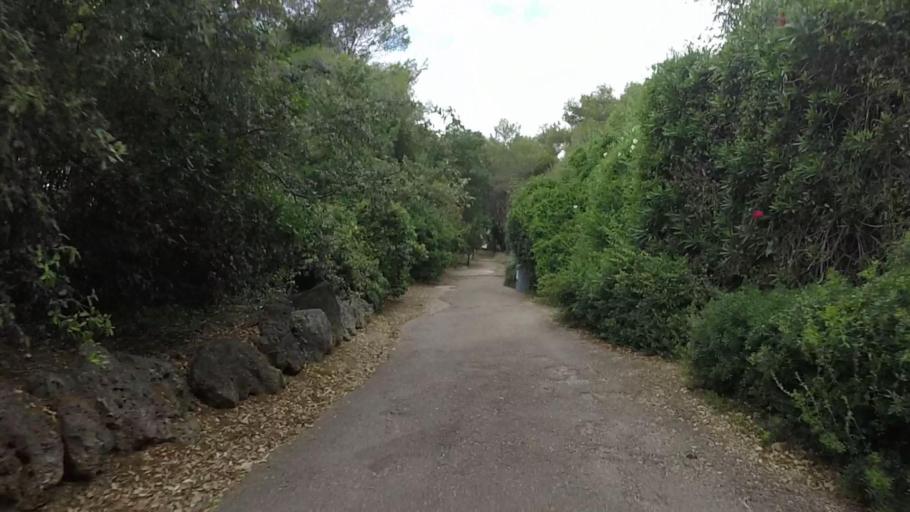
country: FR
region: Provence-Alpes-Cote d'Azur
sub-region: Departement des Alpes-Maritimes
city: Biot
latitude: 43.6201
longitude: 7.0817
